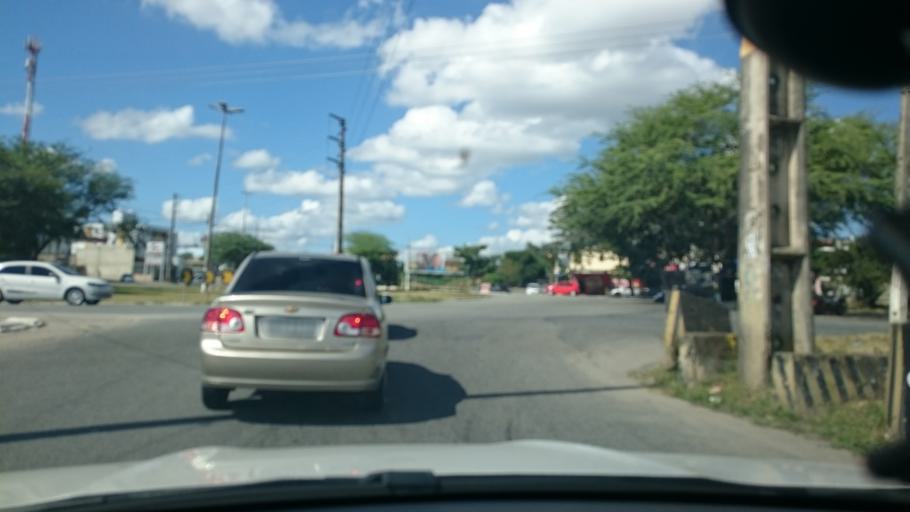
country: BR
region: Paraiba
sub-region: Campina Grande
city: Campina Grande
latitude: -7.2317
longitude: -35.9106
